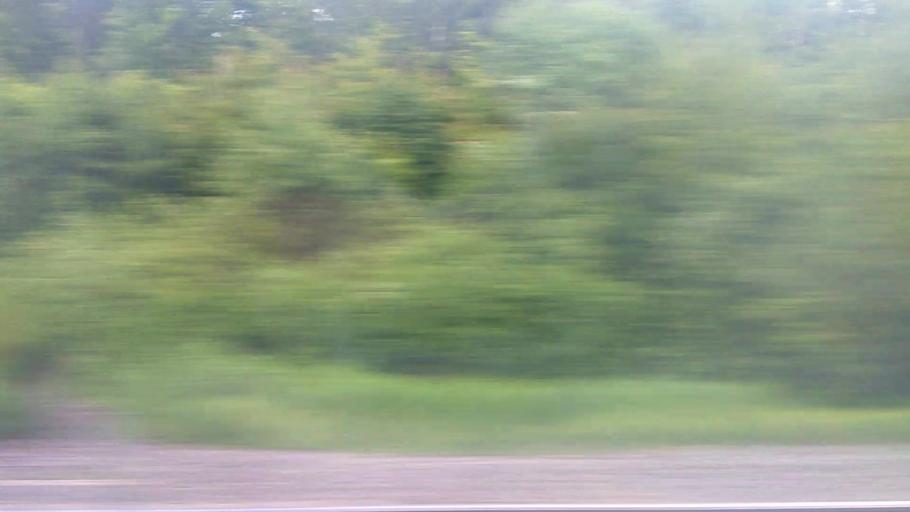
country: RU
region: Moskovskaya
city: Mikhnevo
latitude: 55.0900
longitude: 37.9689
